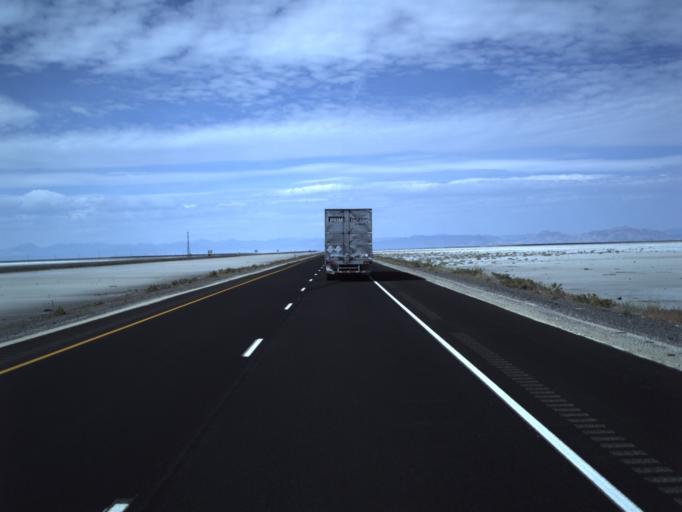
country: US
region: Utah
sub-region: Tooele County
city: Wendover
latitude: 40.7324
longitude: -113.5244
